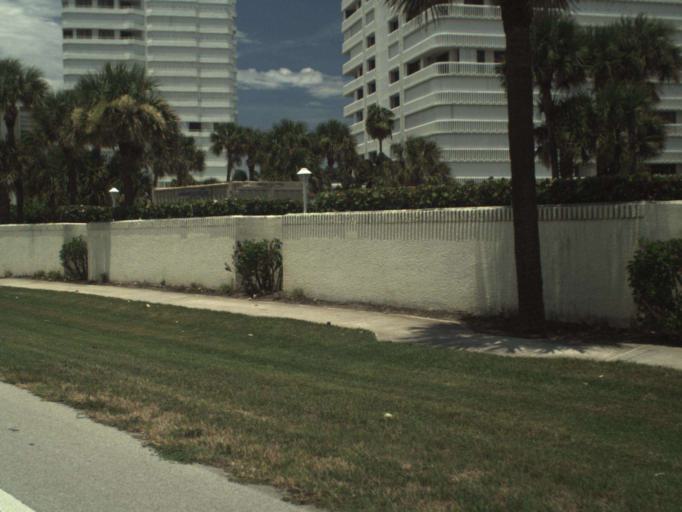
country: US
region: Florida
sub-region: Saint Lucie County
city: Hutchinson Island South
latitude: 27.2817
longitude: -80.2102
